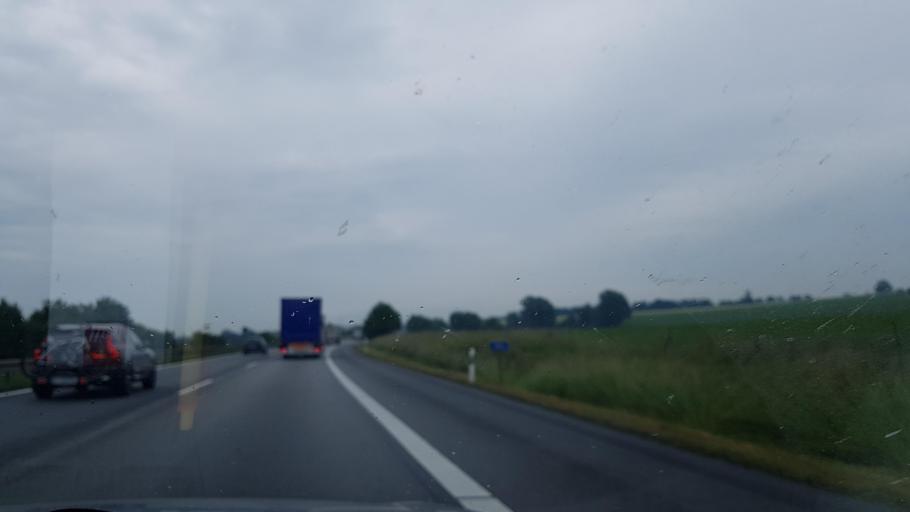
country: DE
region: Saxony
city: Crostwitz
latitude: 51.2035
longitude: 14.2535
